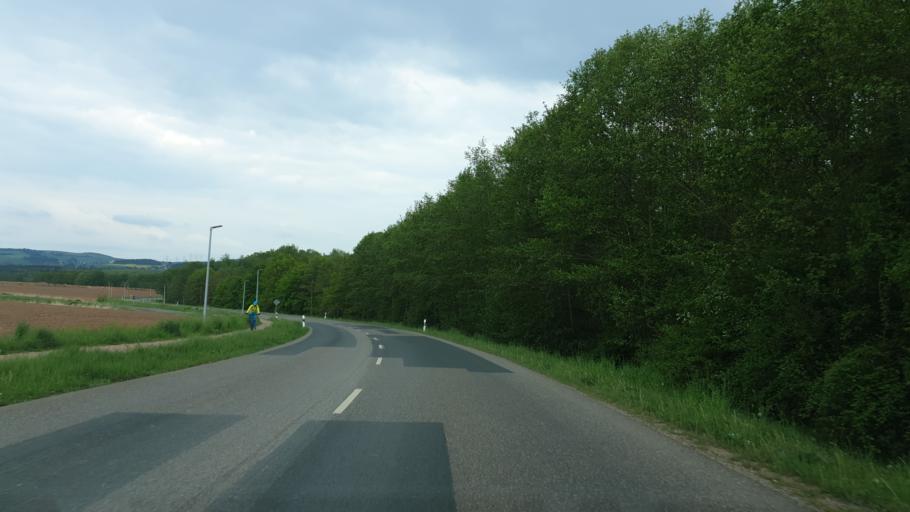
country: DE
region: Saxony
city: Neukirchen
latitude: 50.7695
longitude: 12.8580
